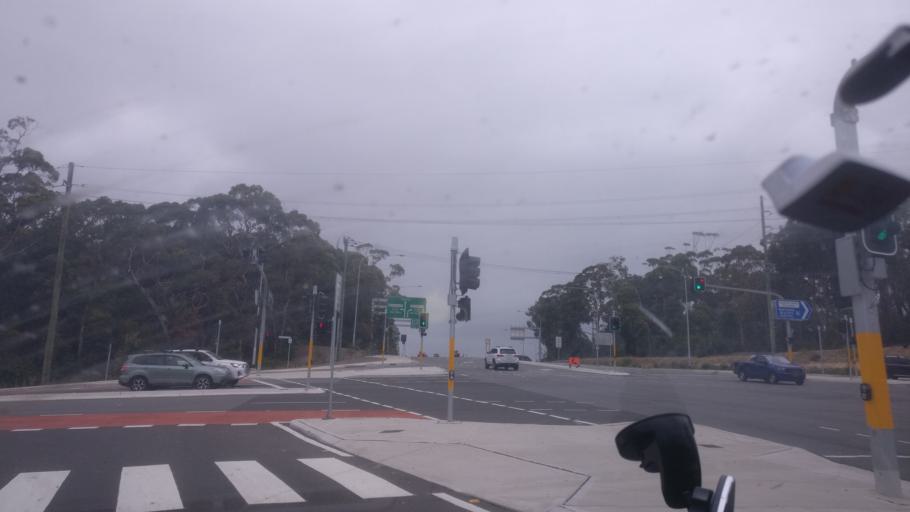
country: AU
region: New South Wales
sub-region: Warringah
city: Allambie Heights
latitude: -33.7497
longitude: 151.2352
